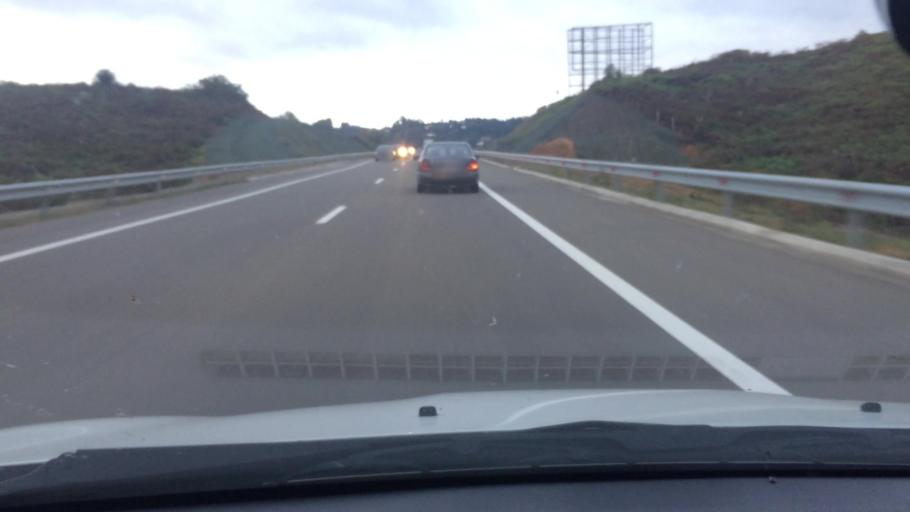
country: GE
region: Ajaria
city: Makhinjauri
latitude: 41.7281
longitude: 41.7511
